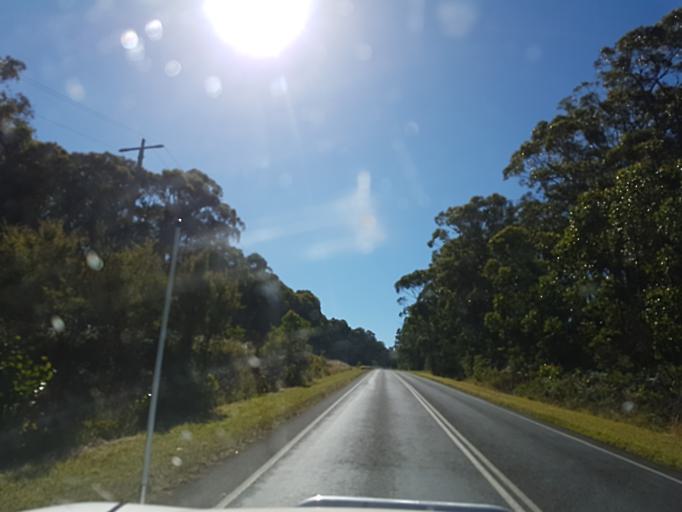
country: AU
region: Victoria
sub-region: Colac-Otway
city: Colac
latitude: -38.4569
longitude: 143.5863
